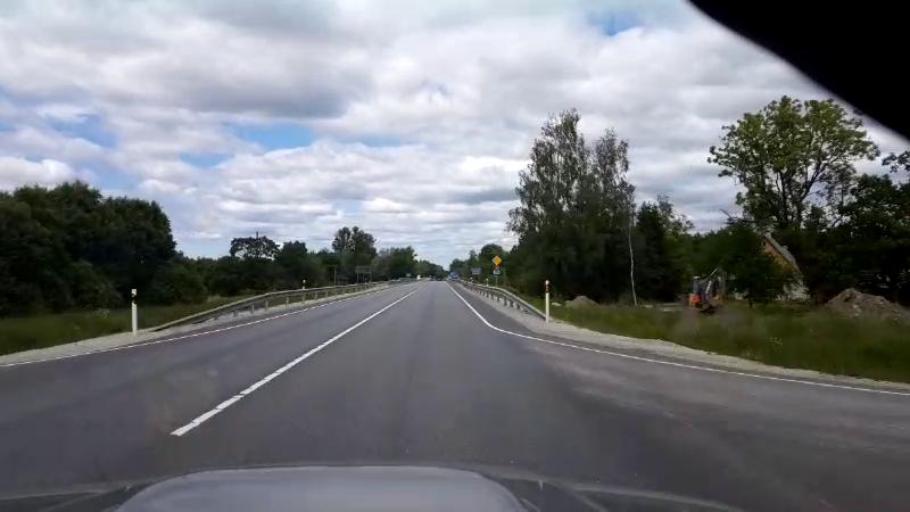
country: EE
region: Raplamaa
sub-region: Maerjamaa vald
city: Marjamaa
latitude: 58.8087
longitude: 24.4126
